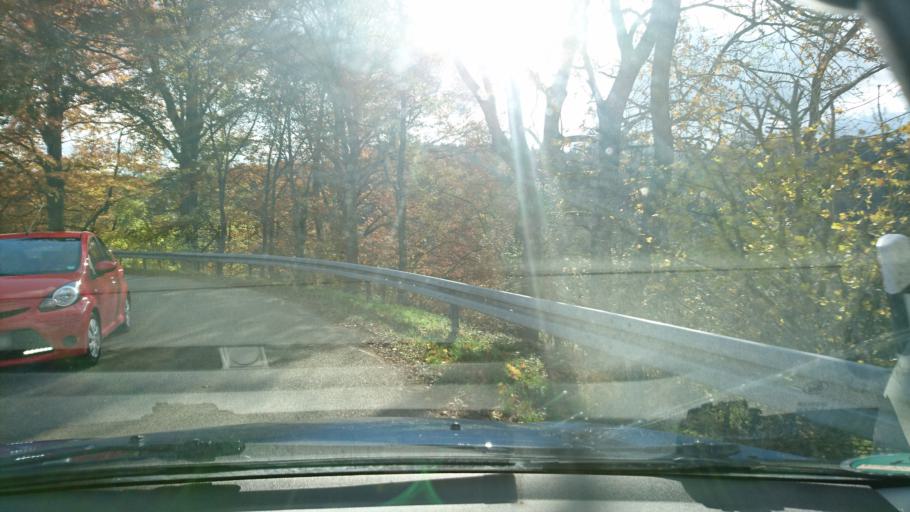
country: DE
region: Baden-Wuerttemberg
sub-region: Regierungsbezirk Stuttgart
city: Heuchlingen
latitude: 48.8788
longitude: 9.9654
